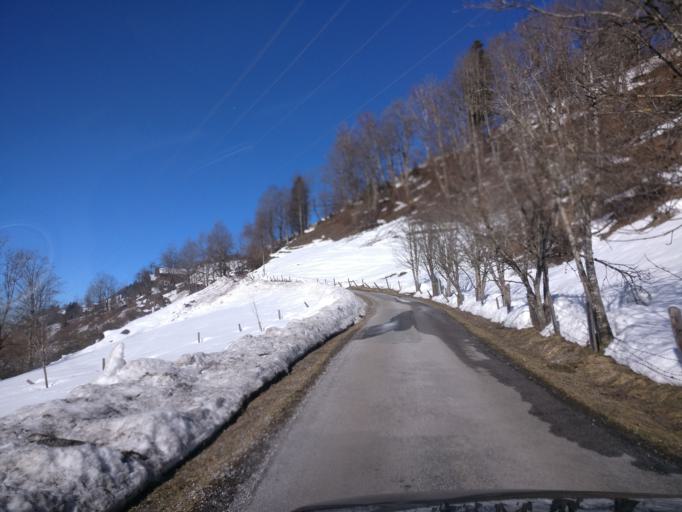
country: AT
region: Salzburg
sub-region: Politischer Bezirk Sankt Johann im Pongau
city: Wagrain
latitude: 47.3369
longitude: 13.2575
